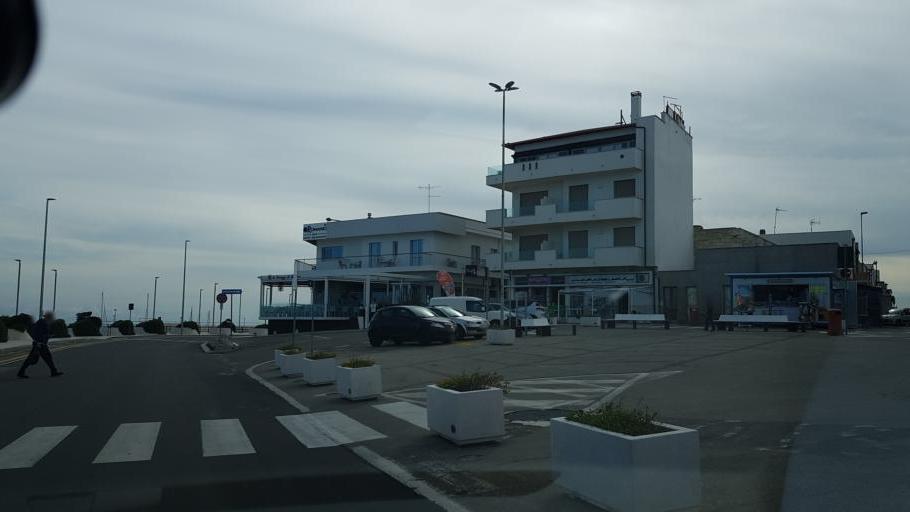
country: IT
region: Apulia
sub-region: Provincia di Lecce
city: Borgagne
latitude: 40.3029
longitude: 18.4032
